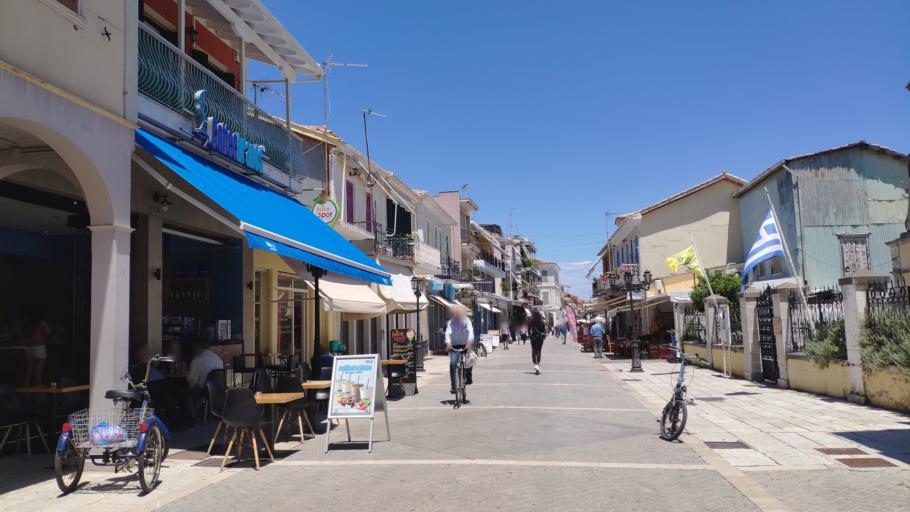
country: GR
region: Ionian Islands
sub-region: Lefkada
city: Lefkada
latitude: 38.8316
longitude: 20.7055
